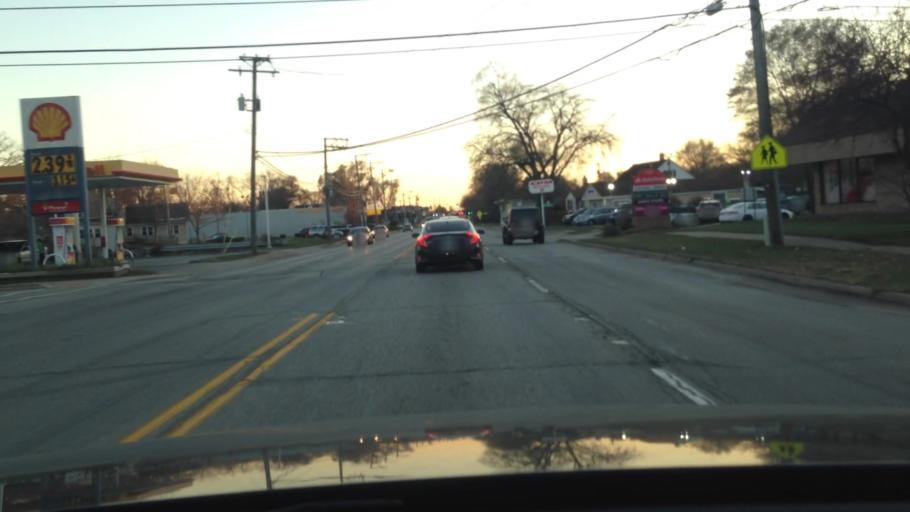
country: US
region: Illinois
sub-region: Kane County
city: Elgin
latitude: 42.0632
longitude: -88.2651
